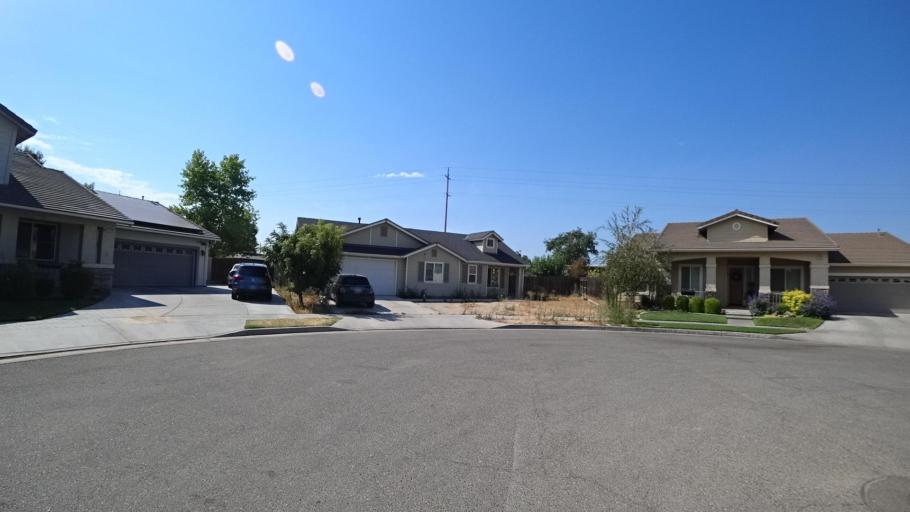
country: US
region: California
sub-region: Fresno County
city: Sunnyside
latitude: 36.7082
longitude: -119.6880
